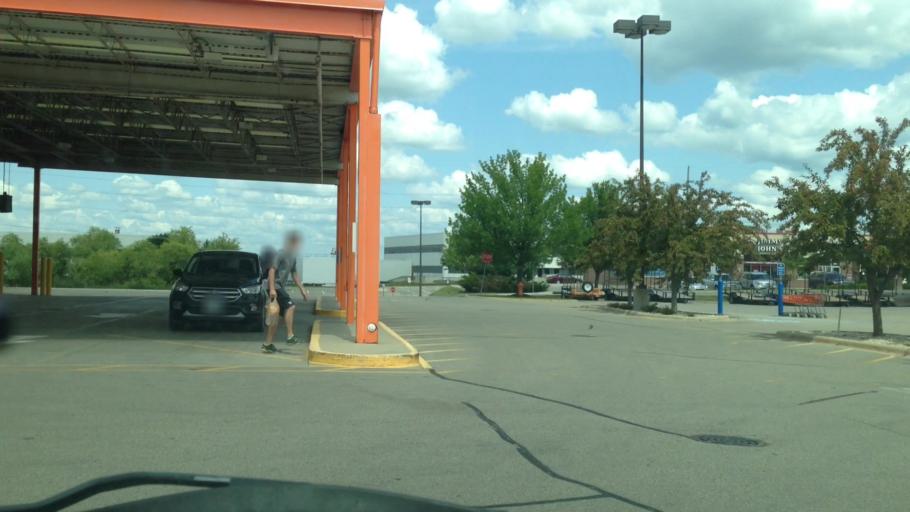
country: US
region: Minnesota
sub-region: Olmsted County
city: Rochester
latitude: 44.0640
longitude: -92.5071
